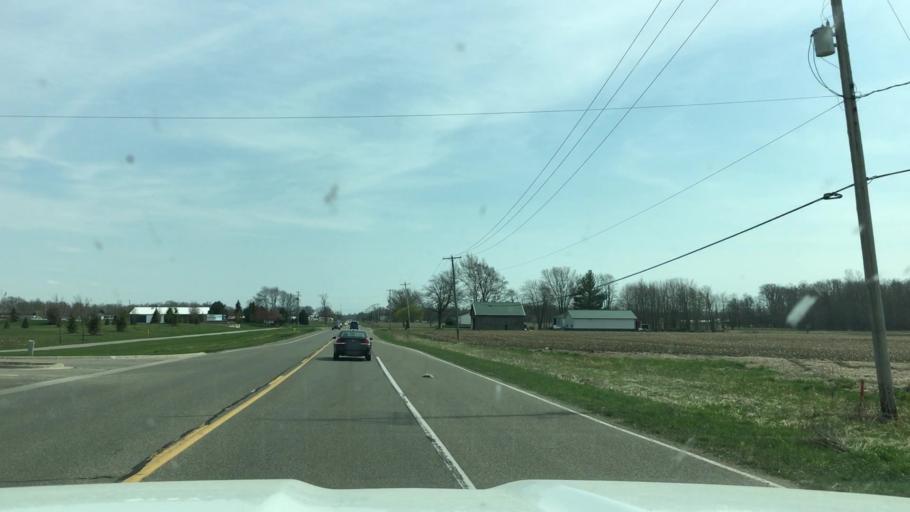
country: US
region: Michigan
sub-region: Ottawa County
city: Hudsonville
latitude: 42.8778
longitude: -85.9013
